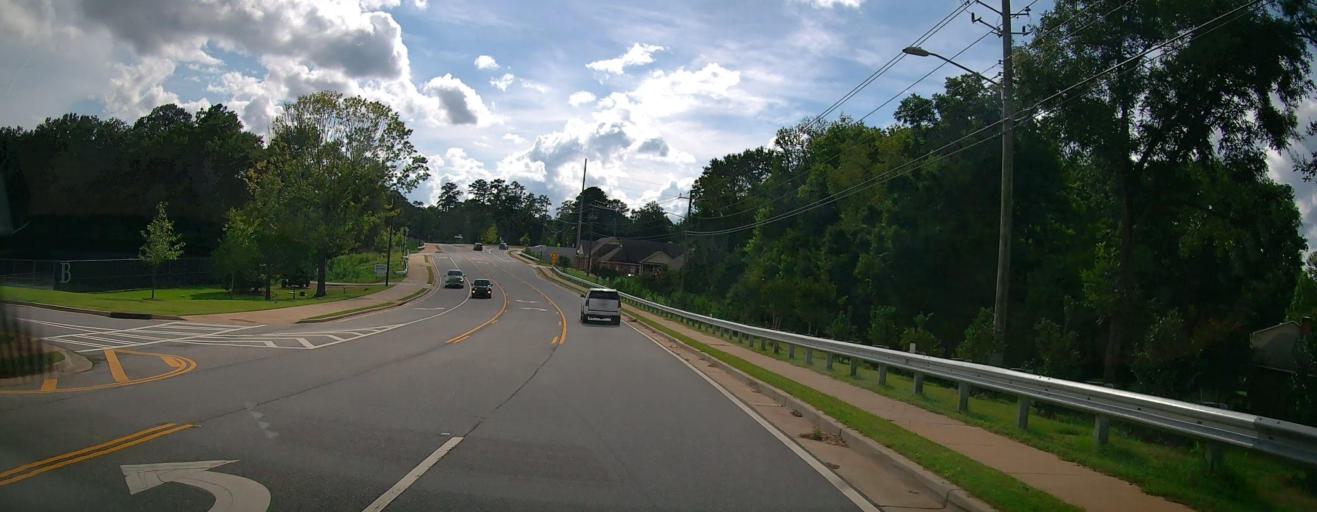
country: US
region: Alabama
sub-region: Russell County
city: Phenix City
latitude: 32.5293
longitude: -84.9896
